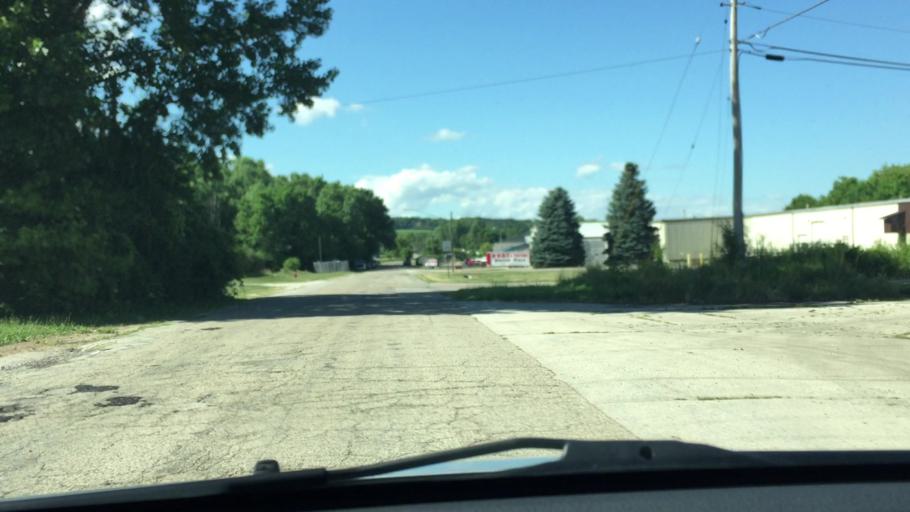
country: US
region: Wisconsin
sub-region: Waukesha County
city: Pewaukee
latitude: 43.0863
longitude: -88.2548
